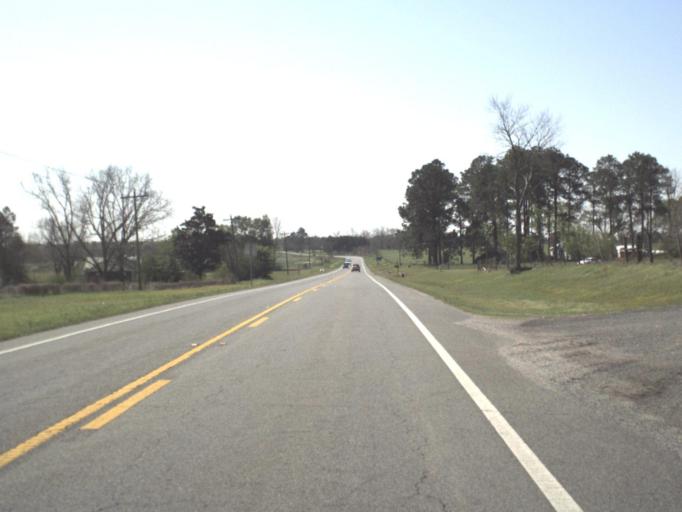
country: US
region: Florida
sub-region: Washington County
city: Chipley
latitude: 30.8325
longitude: -85.5033
